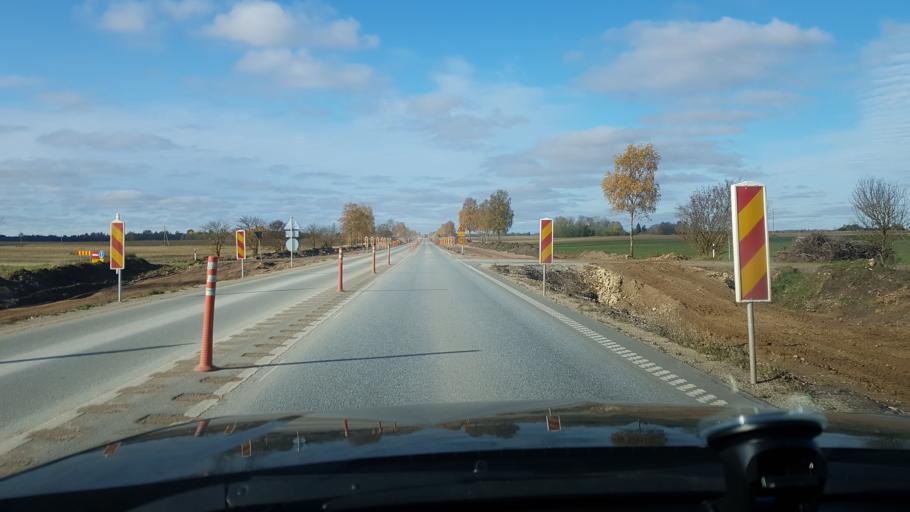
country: EE
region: Laeaene-Virumaa
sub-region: Haljala vald
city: Haljala
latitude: 59.4275
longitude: 26.2376
